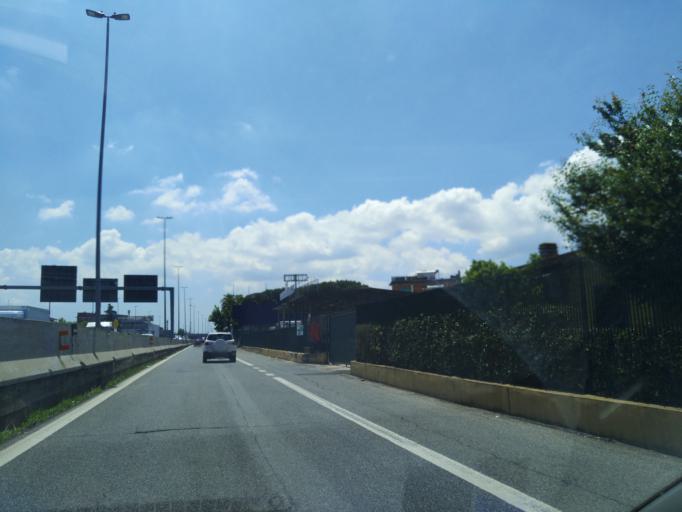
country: IT
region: Latium
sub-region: Citta metropolitana di Roma Capitale
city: Ciampino
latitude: 41.8289
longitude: 12.5844
